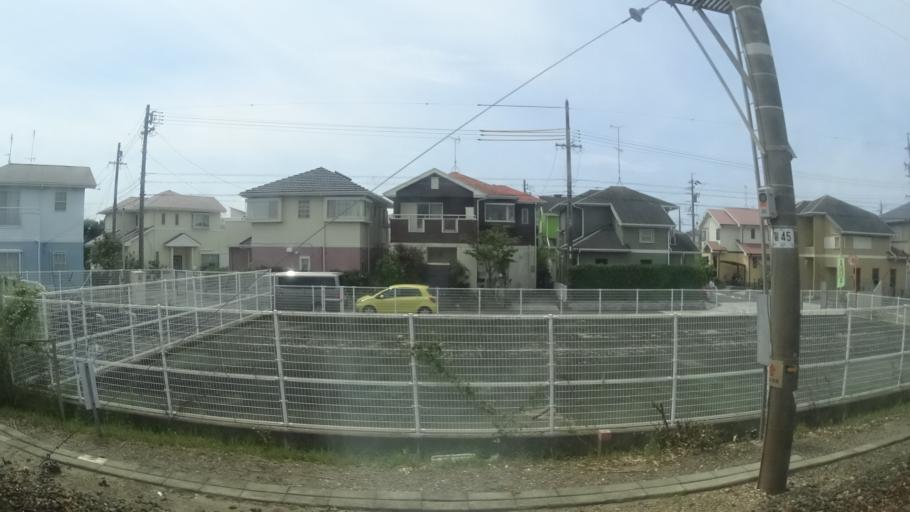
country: JP
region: Shizuoka
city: Hamamatsu
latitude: 34.6853
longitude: 137.6542
